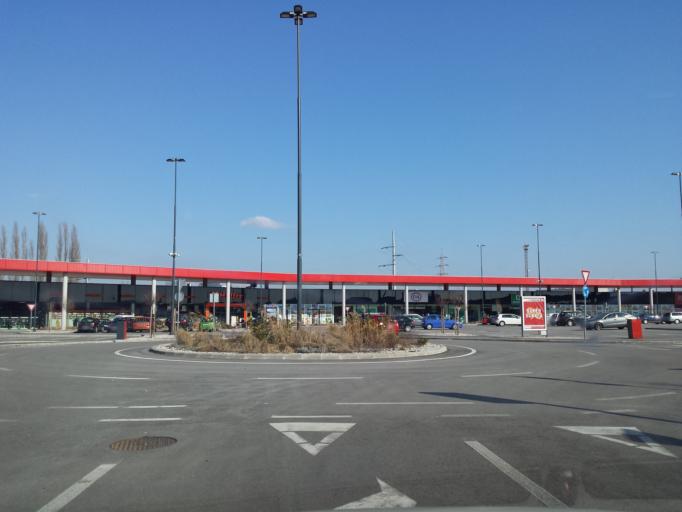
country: HR
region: Grad Zagreb
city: Odra
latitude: 45.7557
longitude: 15.9869
